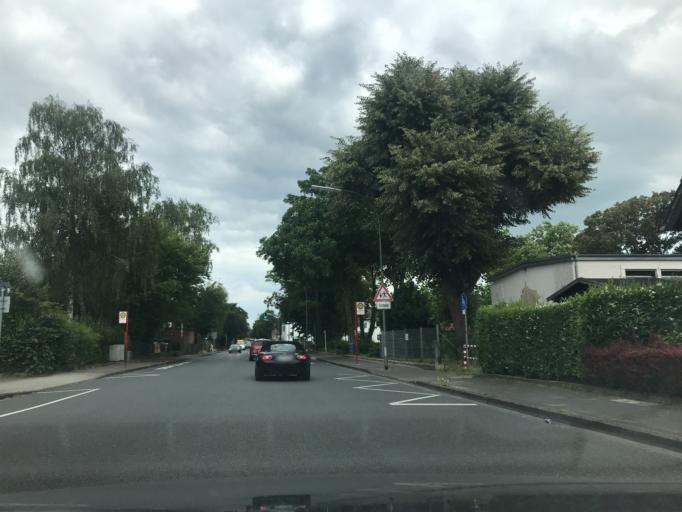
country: DE
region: North Rhine-Westphalia
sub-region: Regierungsbezirk Dusseldorf
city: Neuss
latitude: 51.1632
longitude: 6.6694
